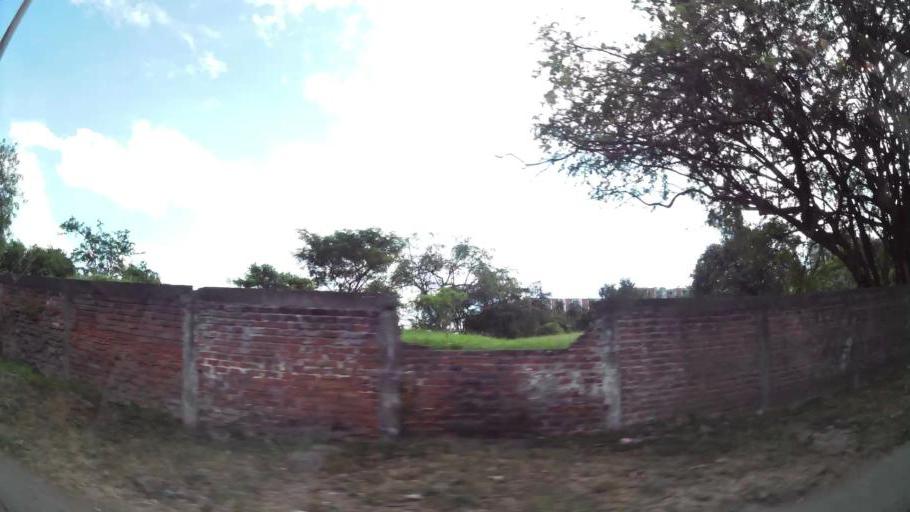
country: CO
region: Valle del Cauca
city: Cali
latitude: 3.4685
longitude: -76.5177
